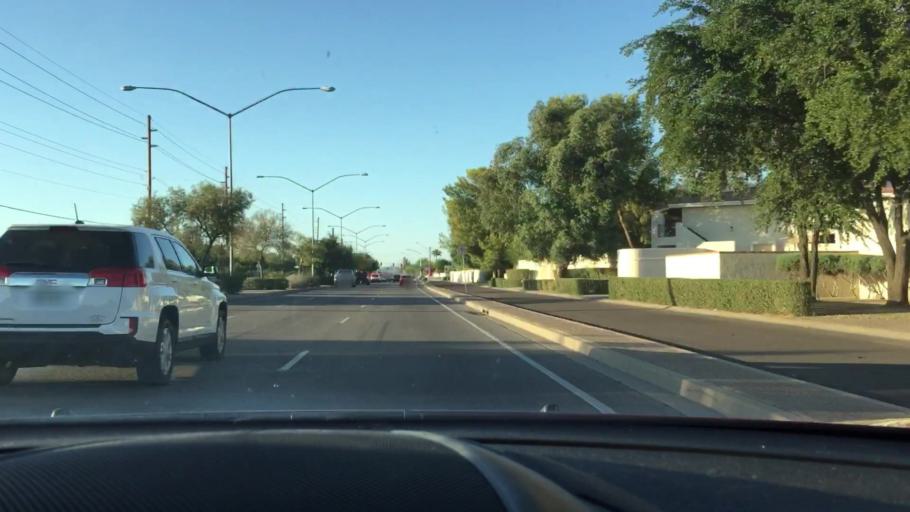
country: US
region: Arizona
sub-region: Maricopa County
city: Gilbert
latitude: 33.4054
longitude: -111.6845
